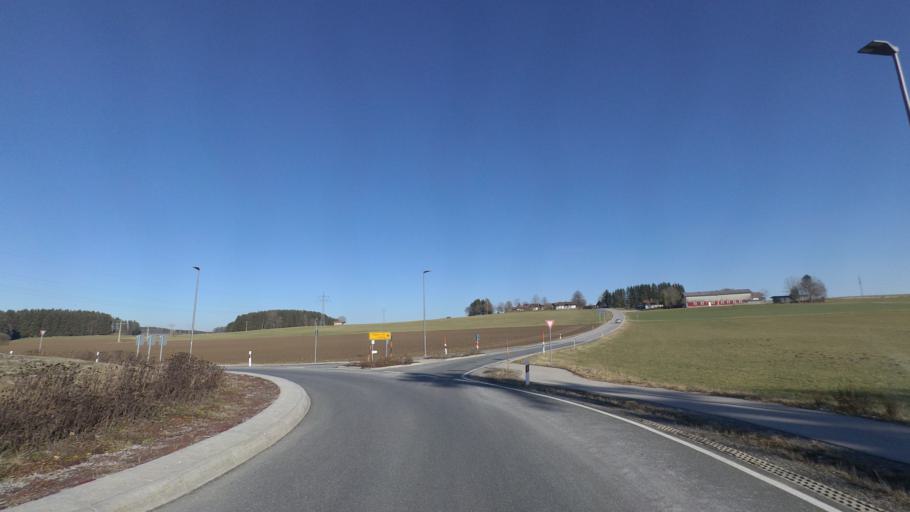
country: DE
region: Bavaria
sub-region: Upper Bavaria
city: Traunreut
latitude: 47.9510
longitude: 12.6191
